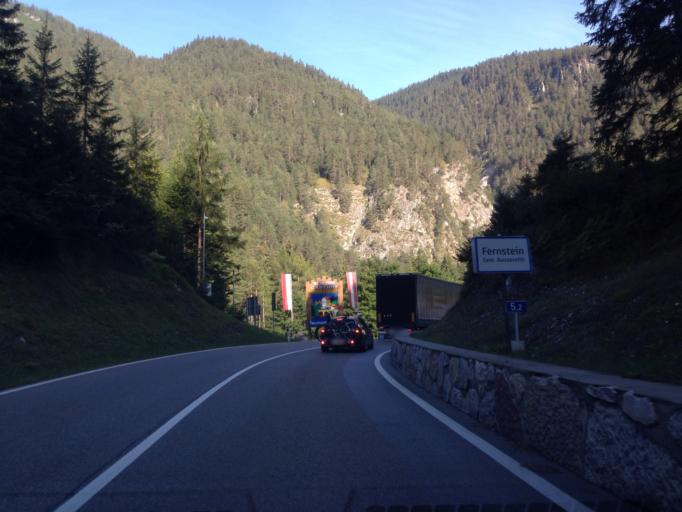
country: AT
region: Tyrol
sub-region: Politischer Bezirk Imst
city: Nassereith
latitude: 47.3432
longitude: 10.8192
